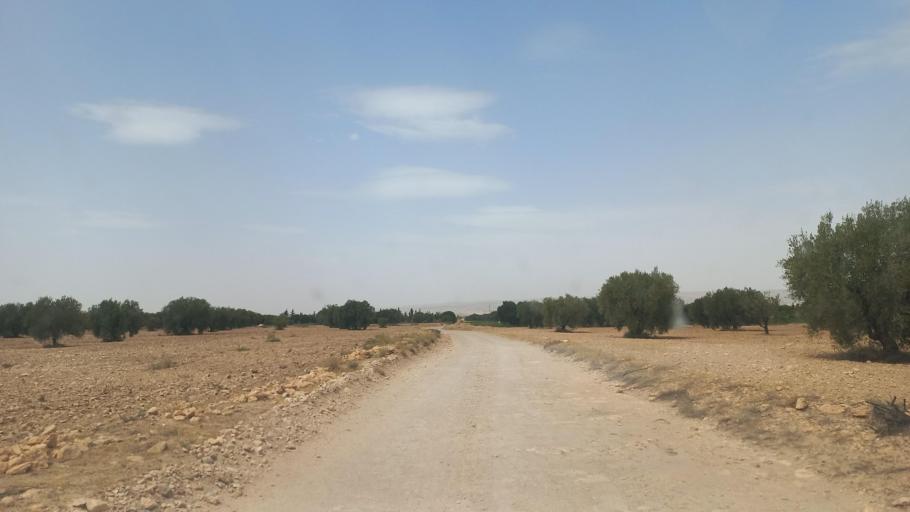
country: TN
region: Al Qasrayn
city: Kasserine
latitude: 35.2566
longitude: 9.0047
